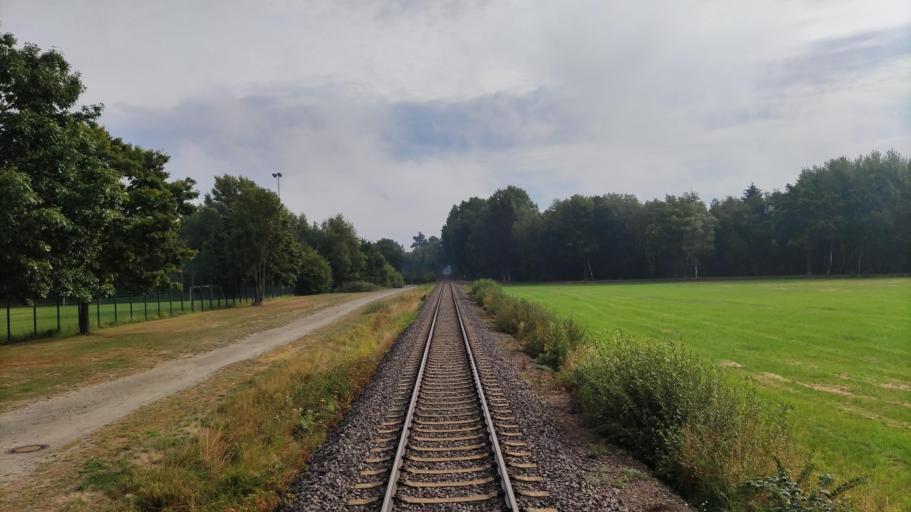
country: DE
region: Lower Saxony
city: Soltau
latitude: 52.9813
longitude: 9.8721
